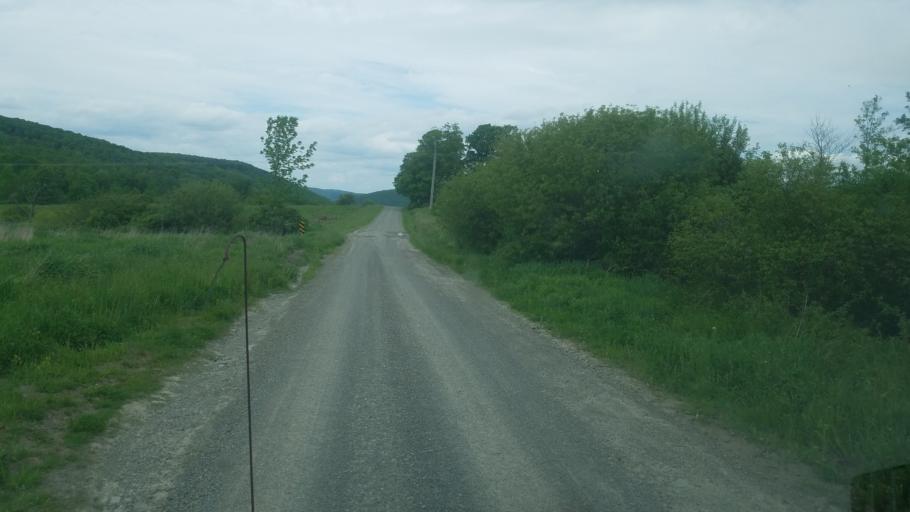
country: US
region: Pennsylvania
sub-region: Tioga County
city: Westfield
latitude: 41.8627
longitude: -77.5986
